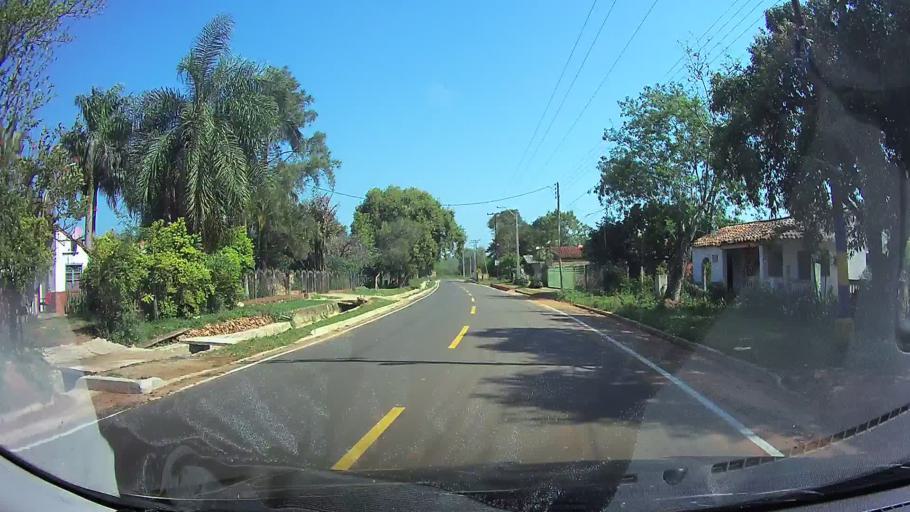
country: PY
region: Central
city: Limpio
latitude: -25.2295
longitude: -57.4903
